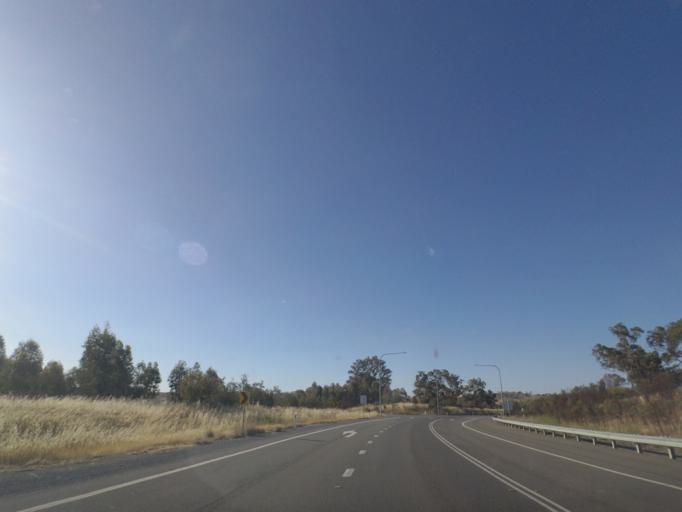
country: AU
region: New South Wales
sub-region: Wagga Wagga
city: Forest Hill
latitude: -35.2628
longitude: 147.7458
